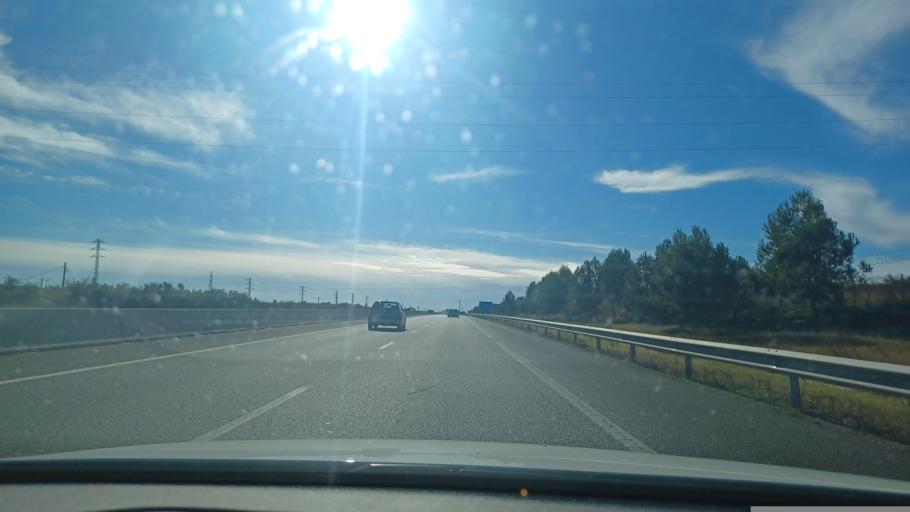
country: ES
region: Catalonia
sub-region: Provincia de Tarragona
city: La Selva
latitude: 41.2317
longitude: 1.1628
